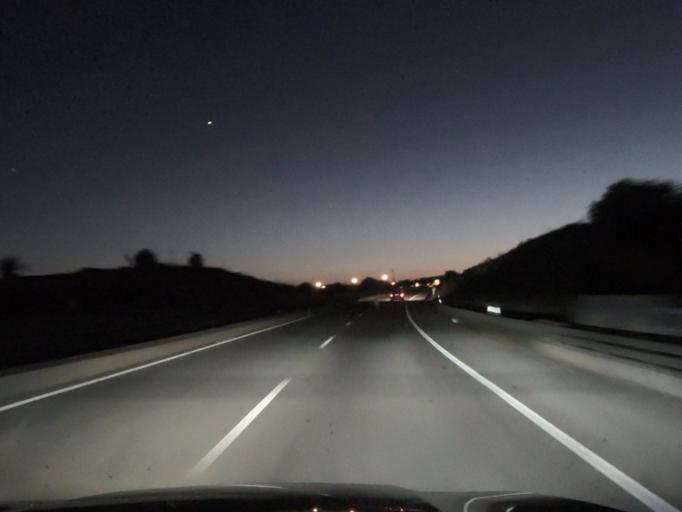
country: PT
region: Faro
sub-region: Loule
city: Loule
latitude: 37.1447
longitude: -8.0340
